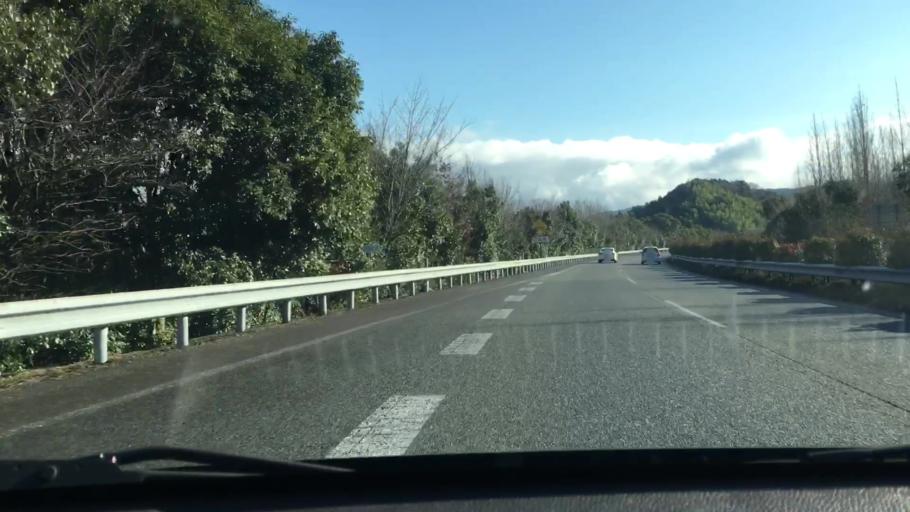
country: JP
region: Kumamoto
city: Hitoyoshi
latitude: 32.1975
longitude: 130.7773
